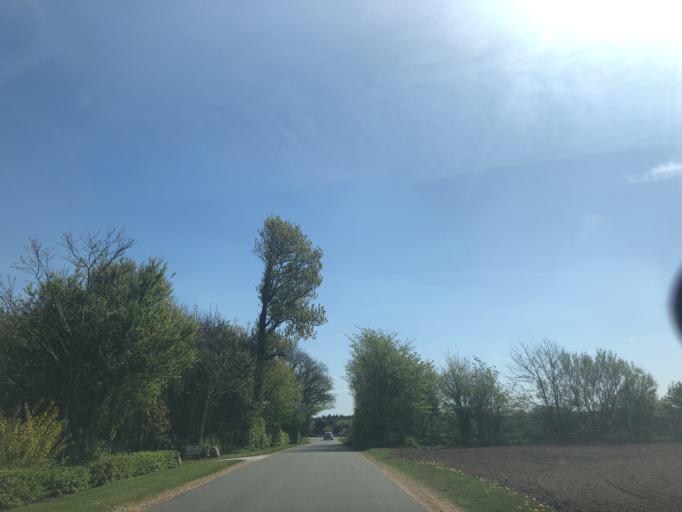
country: DK
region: Central Jutland
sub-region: Holstebro Kommune
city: Vinderup
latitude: 56.5337
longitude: 8.8209
